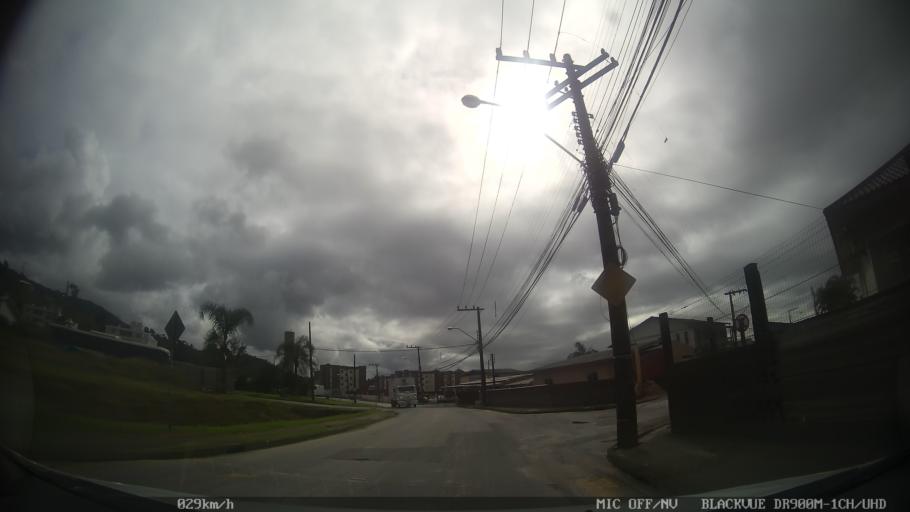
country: BR
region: Santa Catarina
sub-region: Biguacu
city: Biguacu
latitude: -27.5235
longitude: -48.6558
